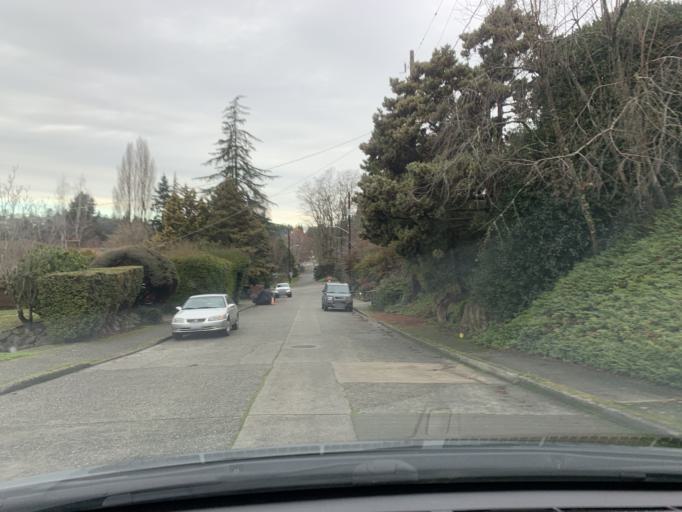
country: US
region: Washington
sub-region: King County
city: White Center
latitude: 47.5541
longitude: -122.3923
